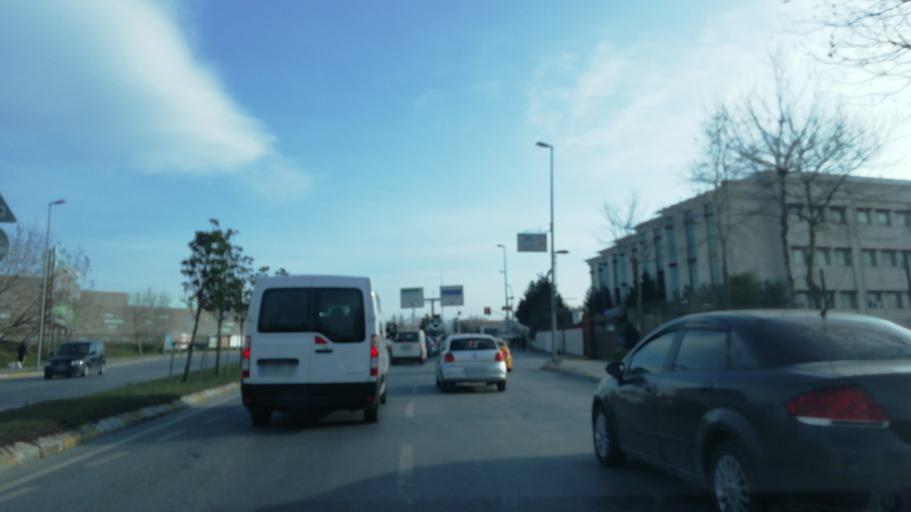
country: TR
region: Istanbul
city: Esenyurt
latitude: 41.0512
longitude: 28.6721
